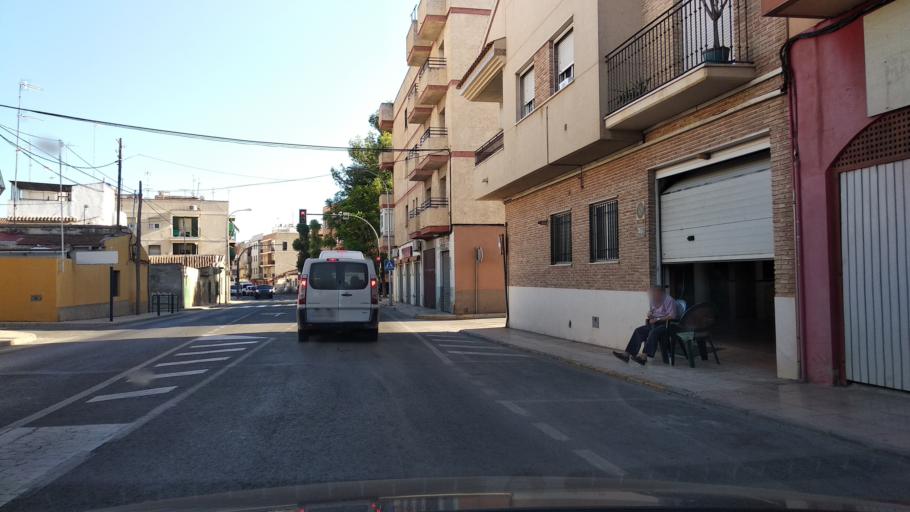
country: ES
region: Murcia
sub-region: Murcia
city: Santomera
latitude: 38.0628
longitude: -1.0538
